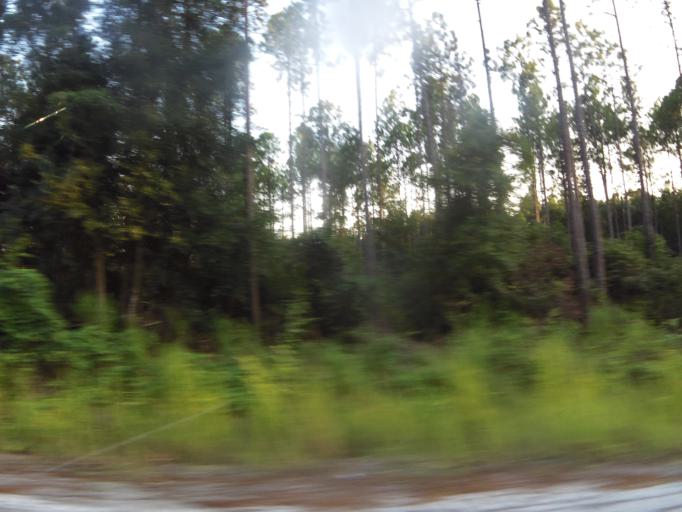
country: US
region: Florida
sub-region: Baker County
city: Macclenny
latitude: 30.3837
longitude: -82.0760
